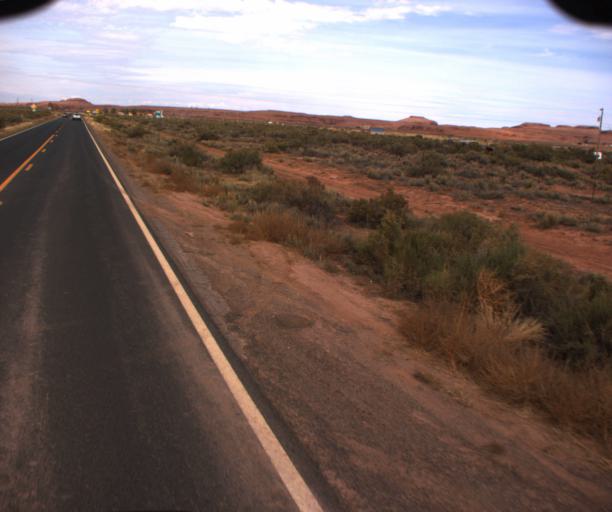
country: US
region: Arizona
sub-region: Apache County
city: Many Farms
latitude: 36.7225
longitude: -109.6286
